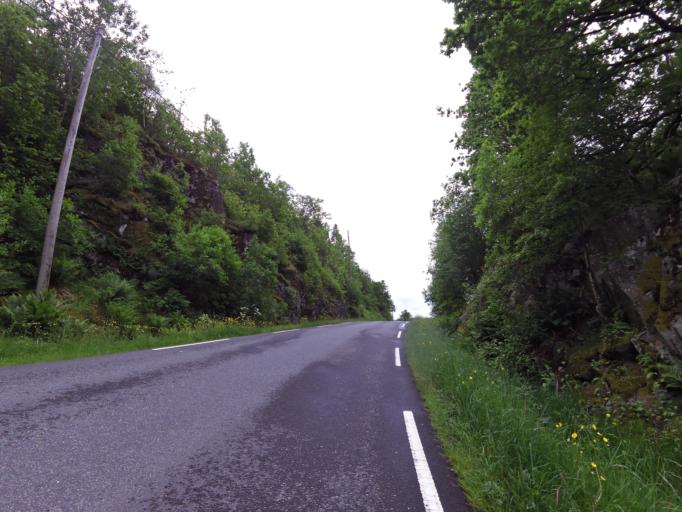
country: NO
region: Vest-Agder
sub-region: Lyngdal
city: Lyngdal
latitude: 58.1038
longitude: 6.9624
